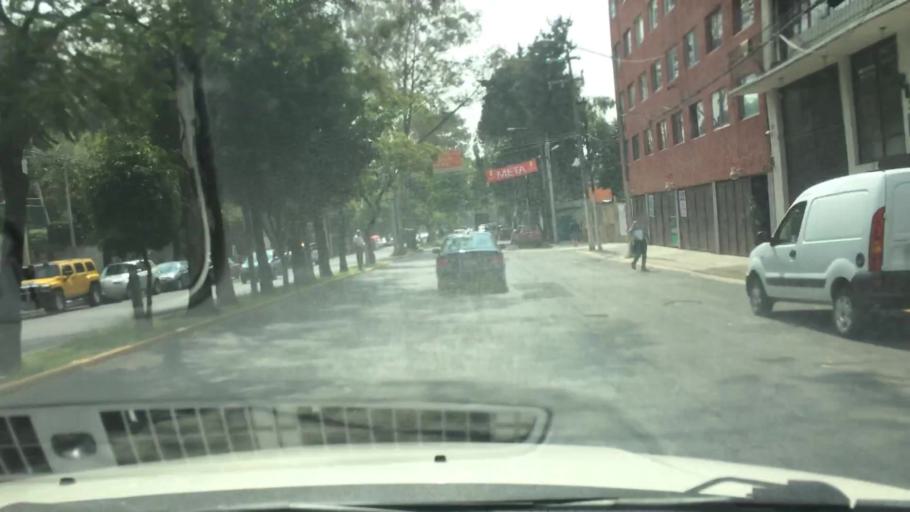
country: MX
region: Mexico City
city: Coyoacan
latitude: 19.3408
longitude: -99.1534
